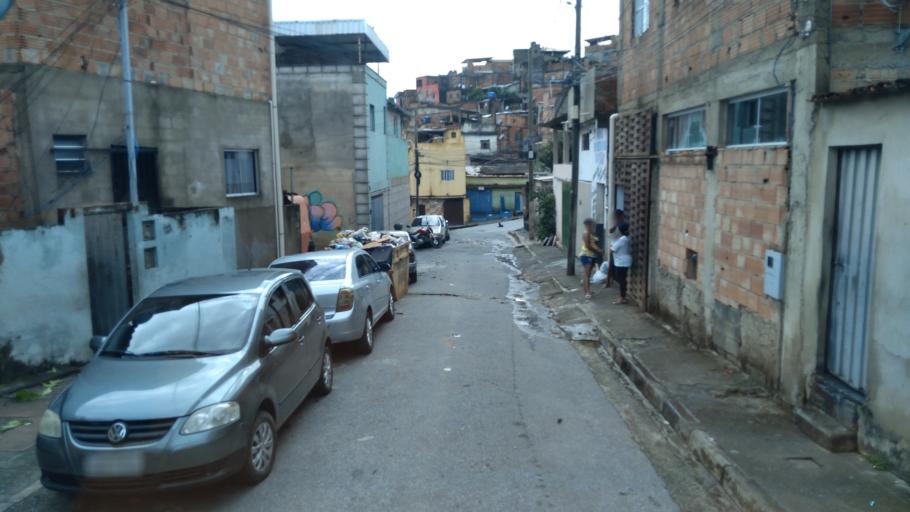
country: BR
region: Minas Gerais
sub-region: Belo Horizonte
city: Belo Horizonte
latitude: -19.9056
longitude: -43.8918
